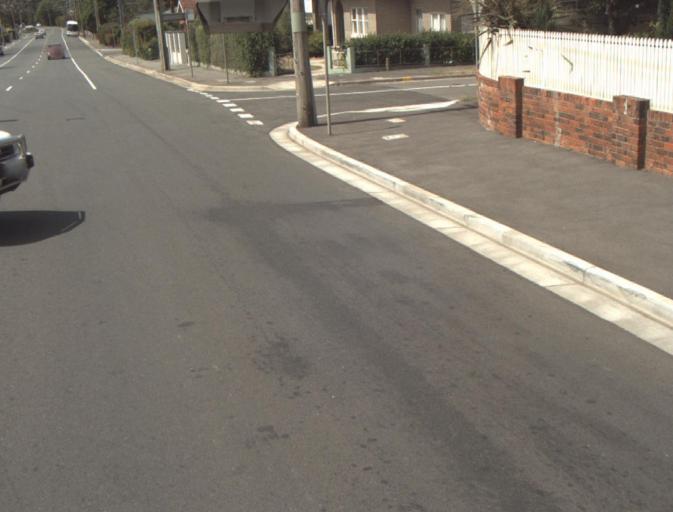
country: AU
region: Tasmania
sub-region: Launceston
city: Newstead
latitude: -41.4419
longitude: 147.1618
